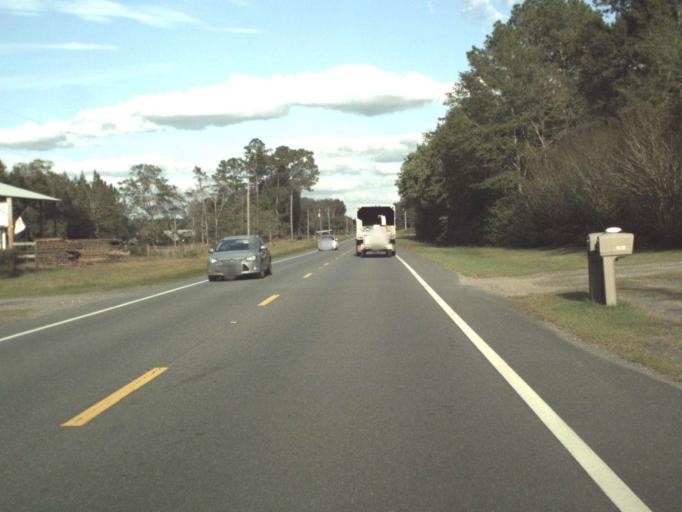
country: US
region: Florida
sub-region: Holmes County
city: Bonifay
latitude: 30.6484
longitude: -85.6801
